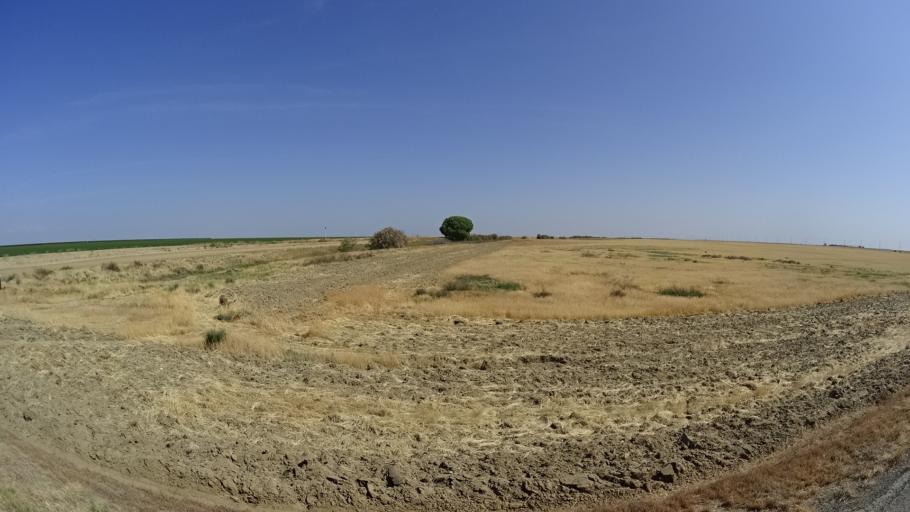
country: US
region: California
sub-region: Kings County
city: Kettleman City
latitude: 36.0363
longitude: -119.9671
